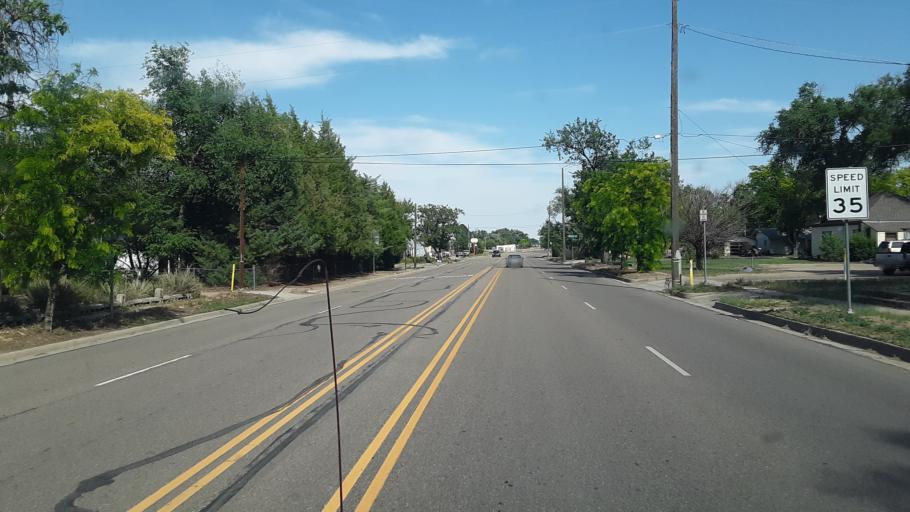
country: US
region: Colorado
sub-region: Otero County
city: Rocky Ford
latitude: 38.1073
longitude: -103.8652
